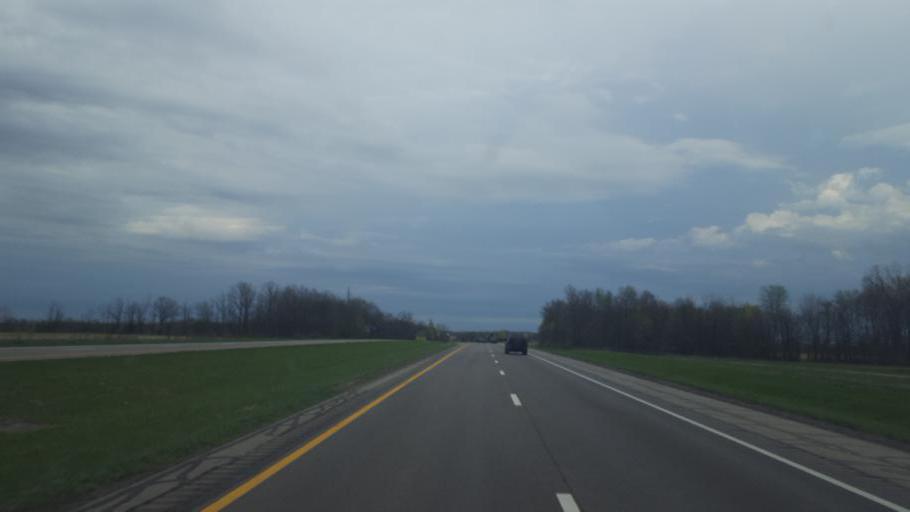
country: US
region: Ohio
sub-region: Crawford County
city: Crestline
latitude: 40.7624
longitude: -82.7344
